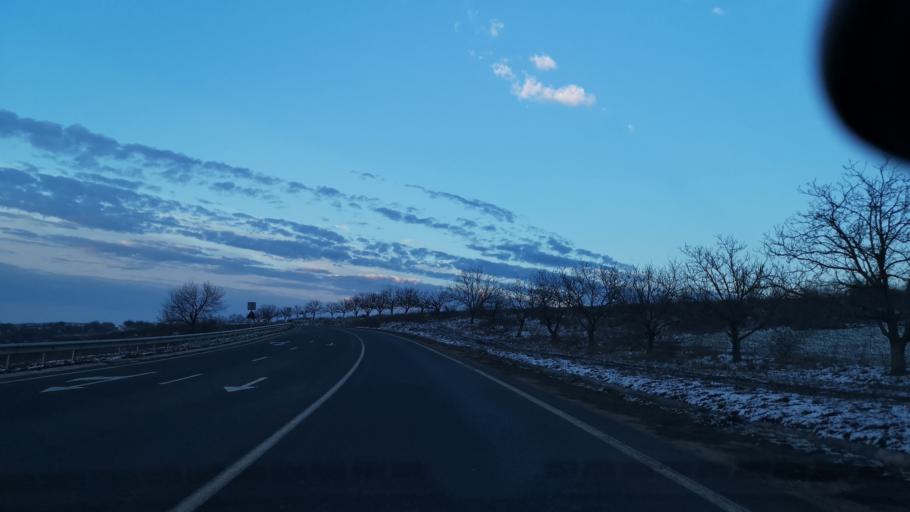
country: MD
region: Rezina
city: Saharna
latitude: 47.6001
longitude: 28.8318
